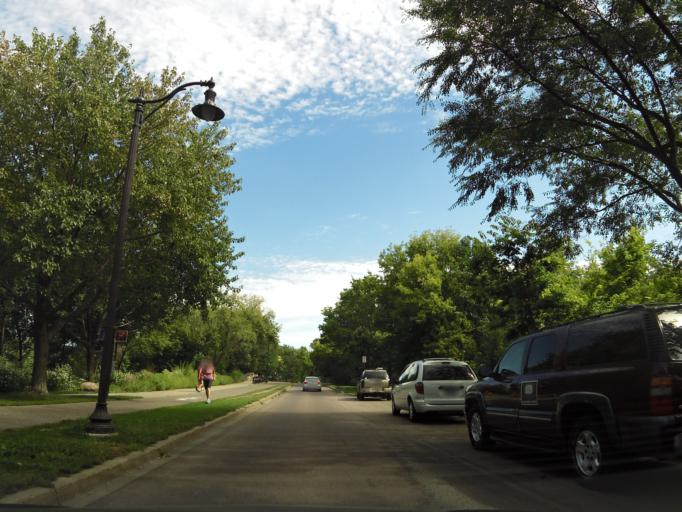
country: US
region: Minnesota
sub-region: Hennepin County
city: Saint Louis Park
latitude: 44.9513
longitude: -93.3076
